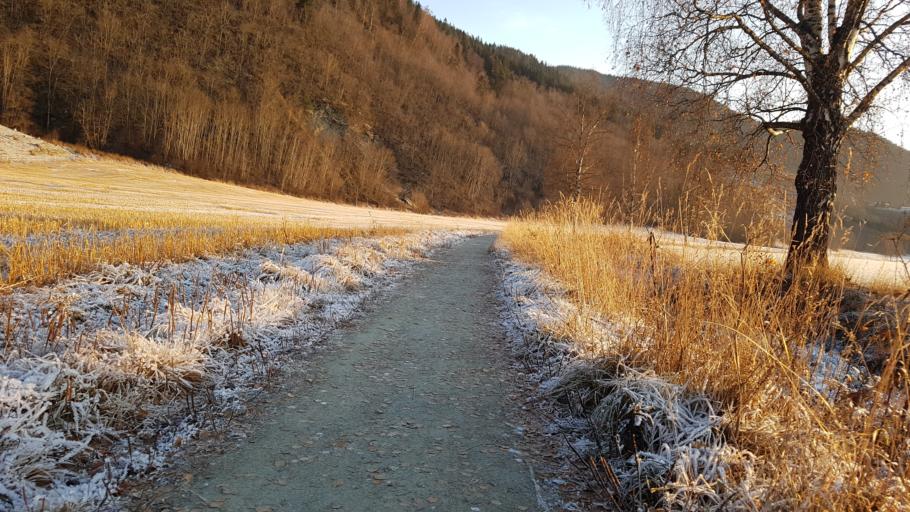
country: NO
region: Sor-Trondelag
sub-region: Melhus
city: Melhus
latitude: 63.2825
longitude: 10.2999
